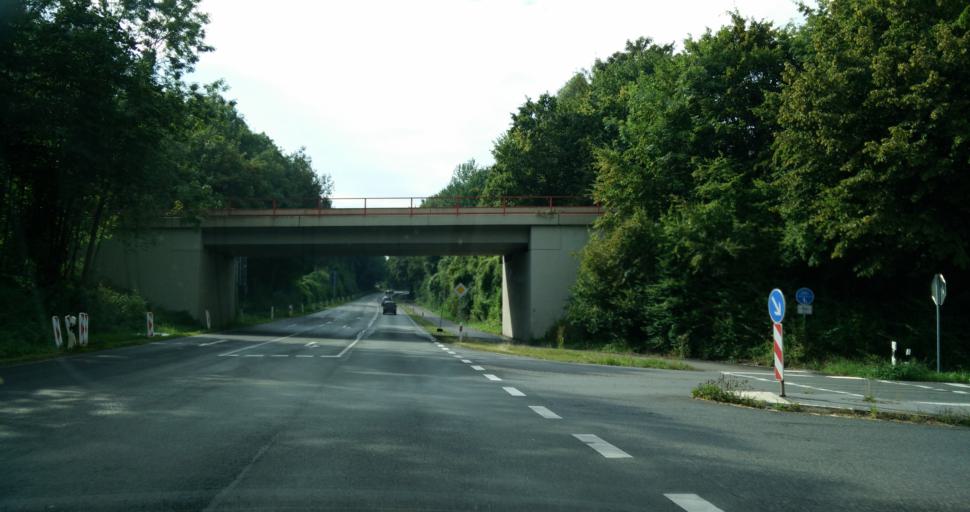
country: DE
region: North Rhine-Westphalia
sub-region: Regierungsbezirk Dusseldorf
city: Mettmann
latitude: 51.2330
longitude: 6.9684
